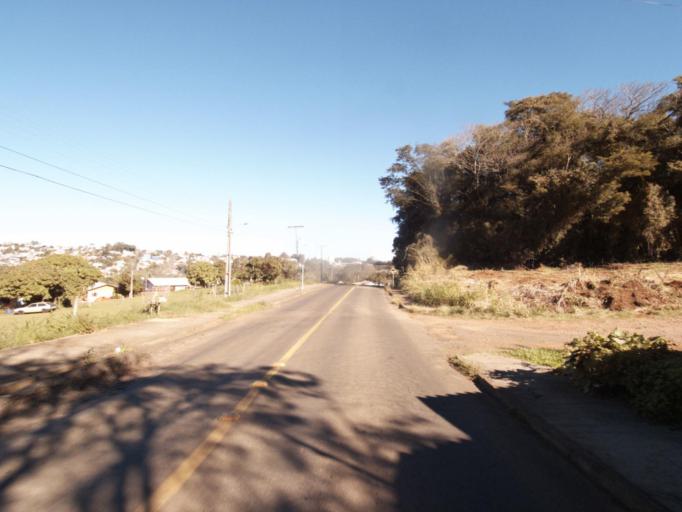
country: AR
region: Misiones
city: Bernardo de Irigoyen
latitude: -26.7105
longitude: -53.5265
